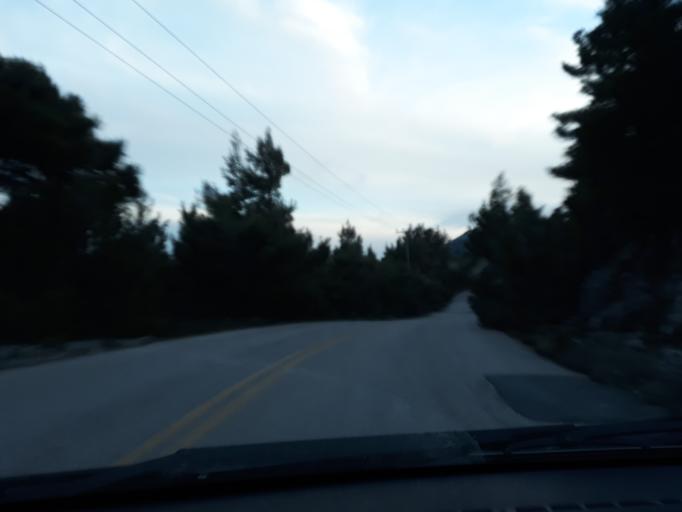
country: GR
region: Attica
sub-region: Nomarchia Anatolikis Attikis
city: Afidnes
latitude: 38.2098
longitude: 23.8002
